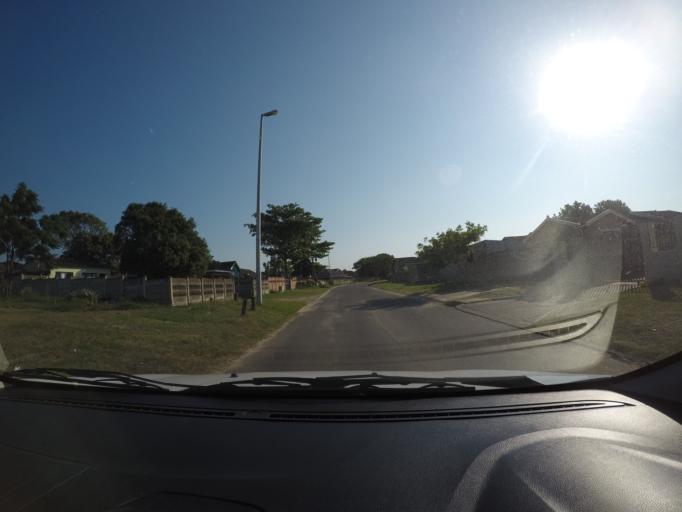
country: ZA
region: KwaZulu-Natal
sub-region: uThungulu District Municipality
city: Richards Bay
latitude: -28.7142
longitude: 32.0374
